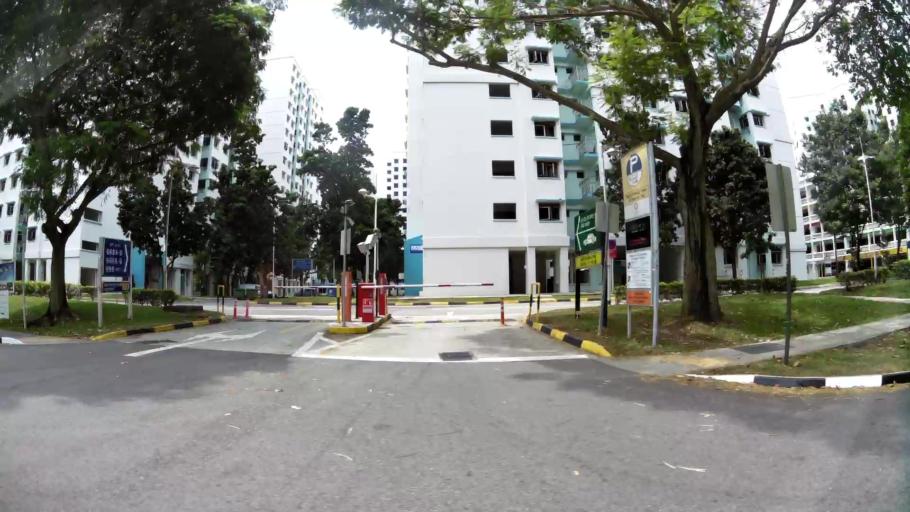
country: MY
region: Johor
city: Johor Bahru
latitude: 1.3420
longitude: 103.7037
